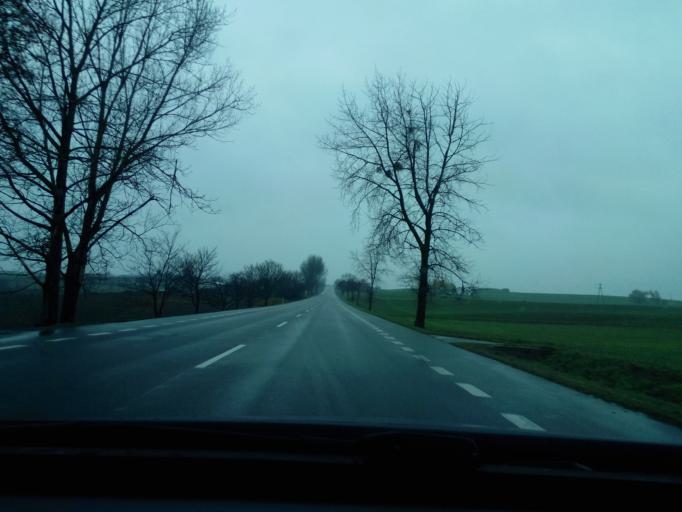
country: PL
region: Pomeranian Voivodeship
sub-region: Powiat tczewski
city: Gniew
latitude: 53.7881
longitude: 18.7776
